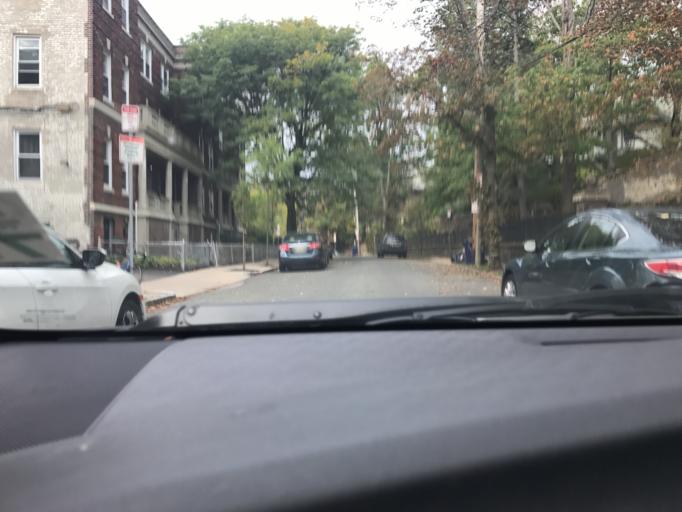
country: US
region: Massachusetts
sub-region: Norfolk County
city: Brookline
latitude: 42.3412
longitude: -71.1437
